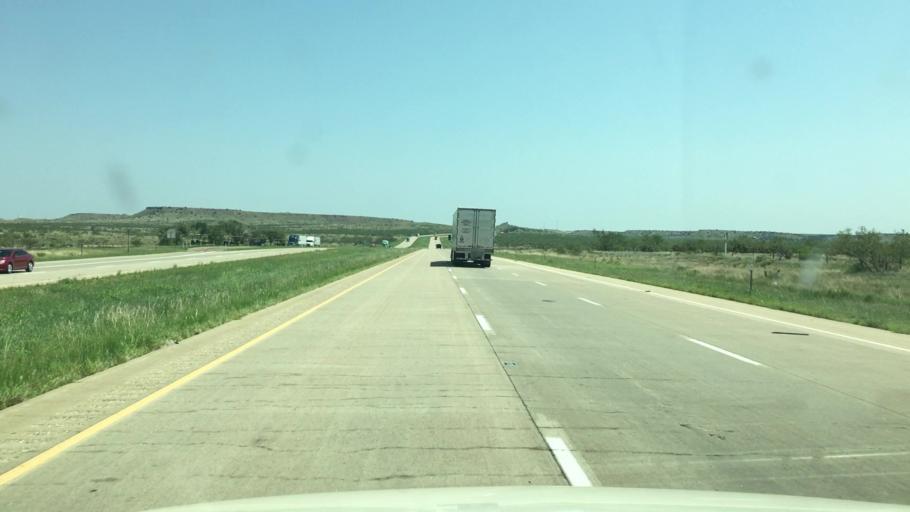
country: US
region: Texas
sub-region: Oldham County
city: Vega
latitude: 35.2395
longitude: -102.8304
